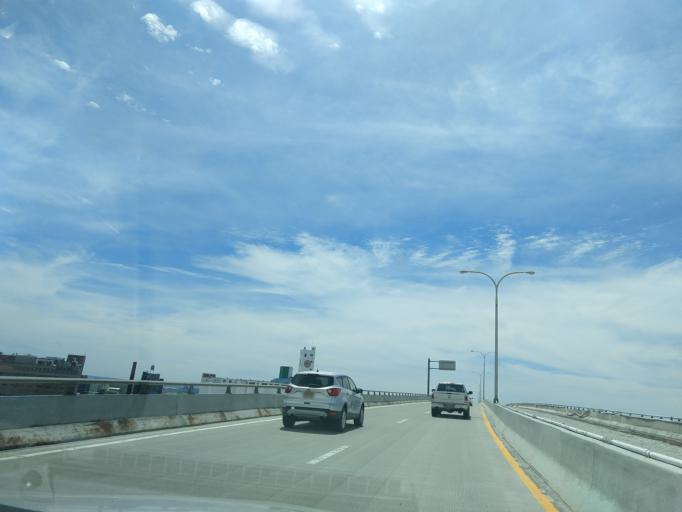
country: US
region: New York
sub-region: Erie County
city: Buffalo
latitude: 42.8751
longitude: -78.8780
